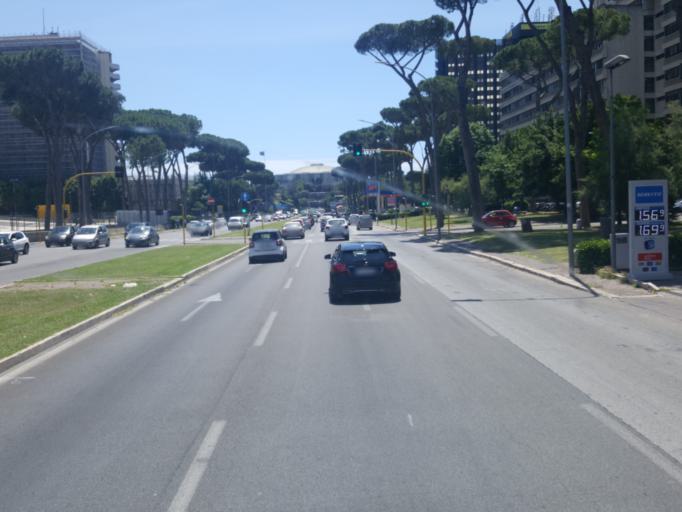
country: IT
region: Latium
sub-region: Citta metropolitana di Roma Capitale
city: Selcetta
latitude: 41.8326
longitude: 12.4702
